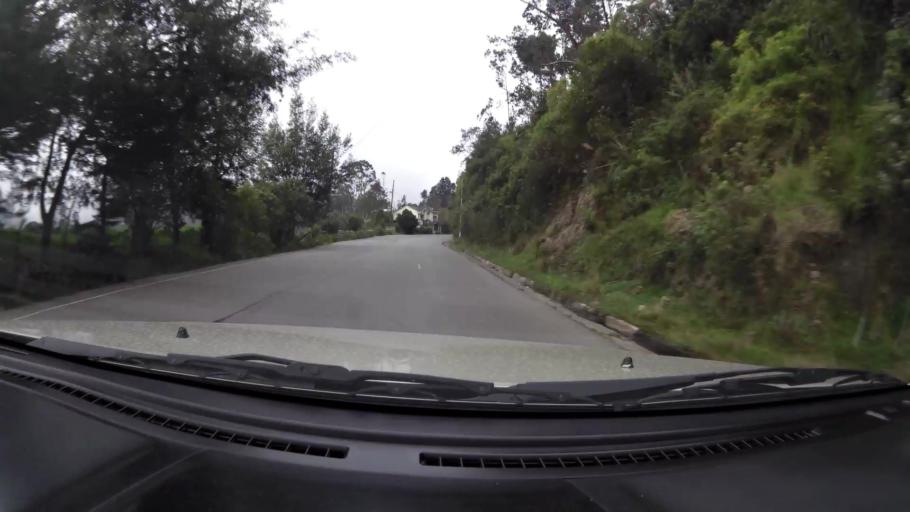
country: EC
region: Canar
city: Canar
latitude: -2.4575
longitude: -79.0044
